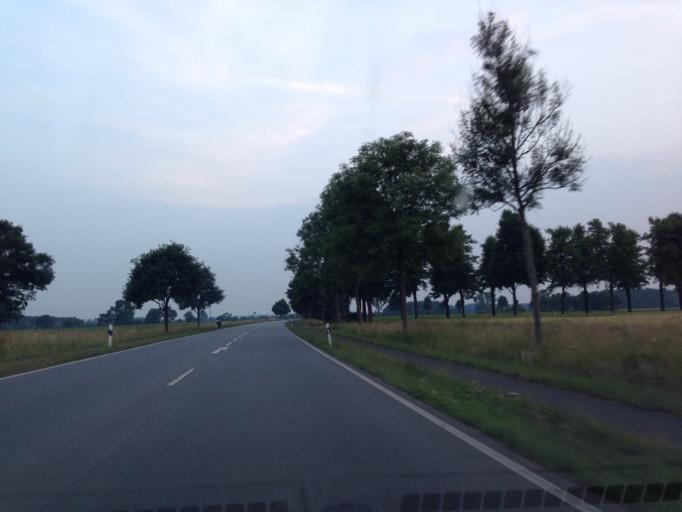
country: DE
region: North Rhine-Westphalia
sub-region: Regierungsbezirk Munster
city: Senden
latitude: 51.8079
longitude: 7.4885
